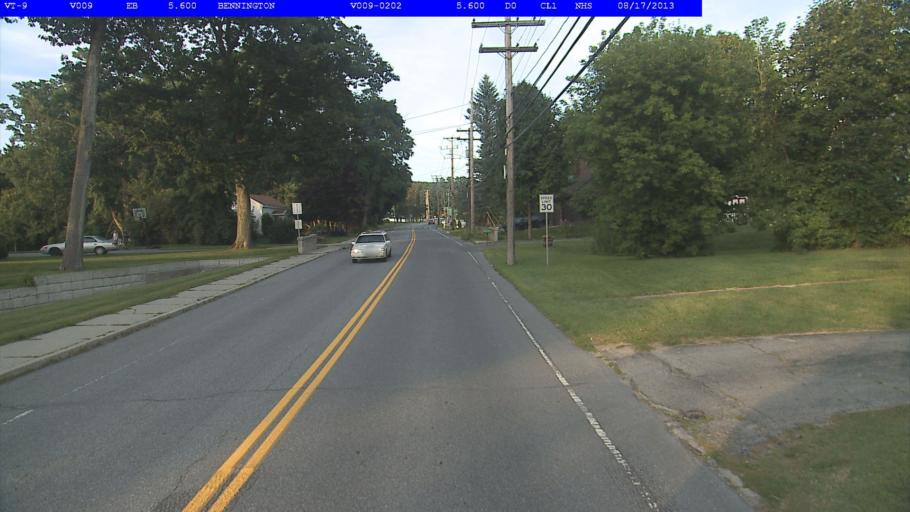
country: US
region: Vermont
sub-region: Bennington County
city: Bennington
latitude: 42.8804
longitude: -73.1740
